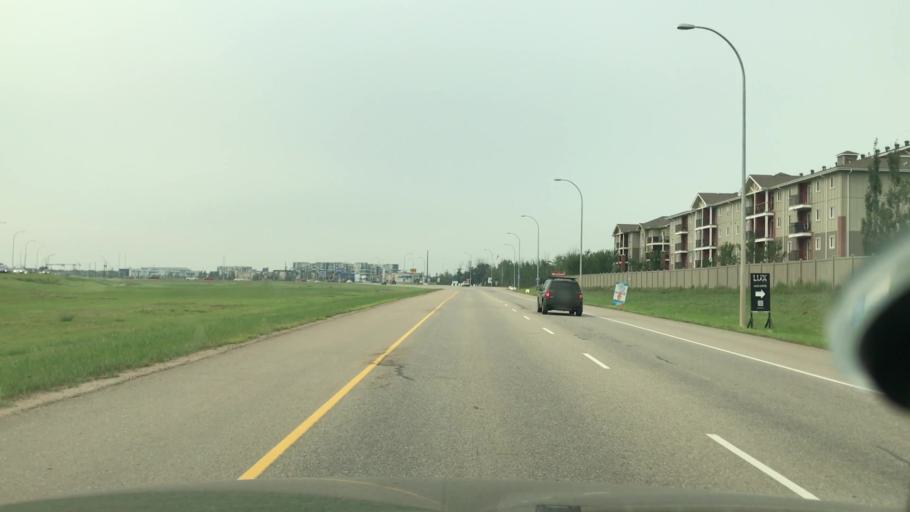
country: CA
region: Alberta
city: Devon
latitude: 53.4407
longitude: -113.6087
